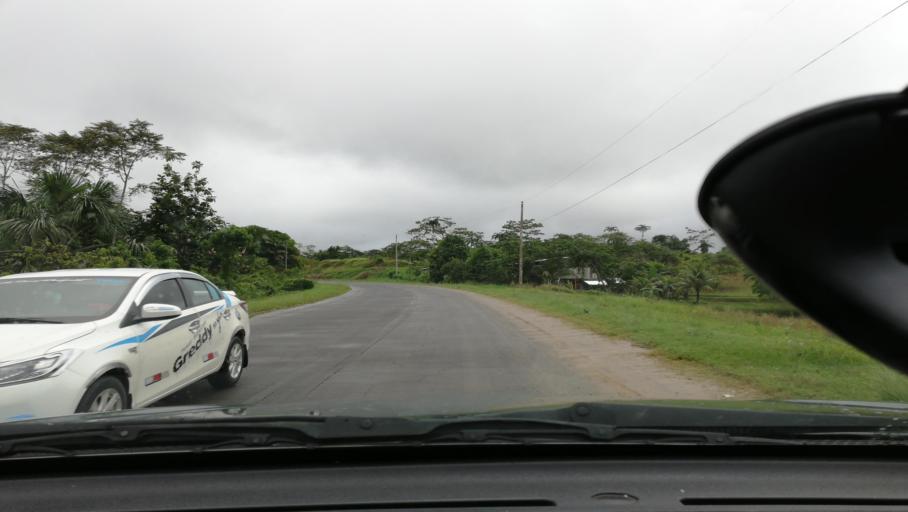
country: PE
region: Loreto
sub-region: Provincia de Loreto
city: Nauta
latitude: -4.2377
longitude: -73.4880
